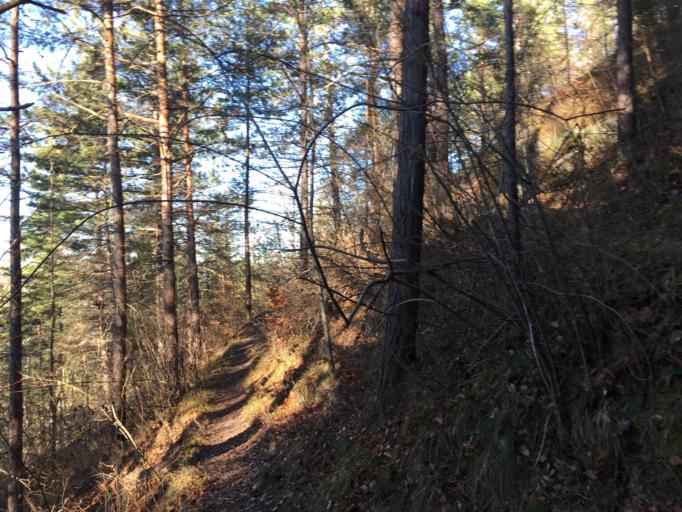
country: DE
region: Thuringia
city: Grosspurschutz
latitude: 50.8049
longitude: 11.6006
